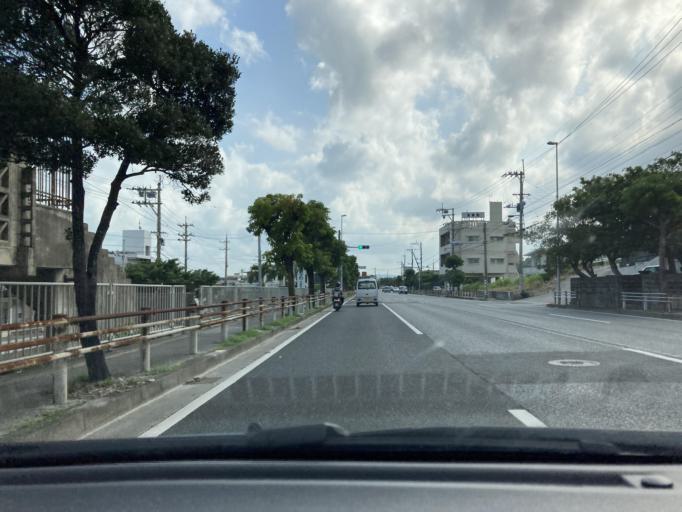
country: JP
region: Okinawa
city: Ginowan
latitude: 26.2668
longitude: 127.7905
